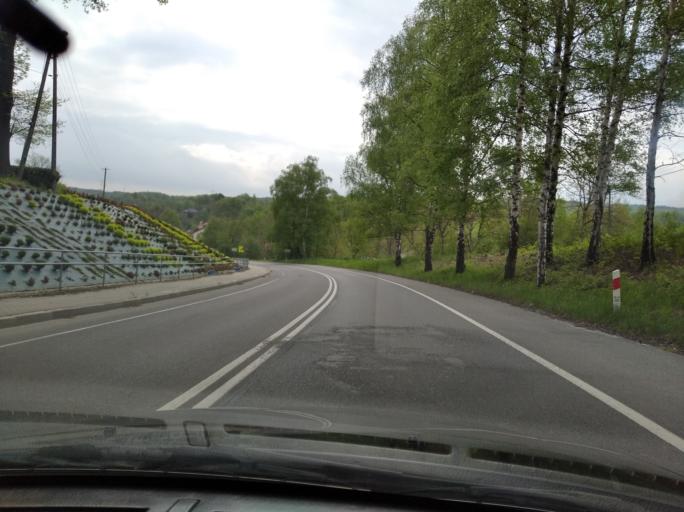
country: PL
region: Lesser Poland Voivodeship
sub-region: Powiat tarnowski
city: Tarnowiec
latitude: 49.9603
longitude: 20.9907
